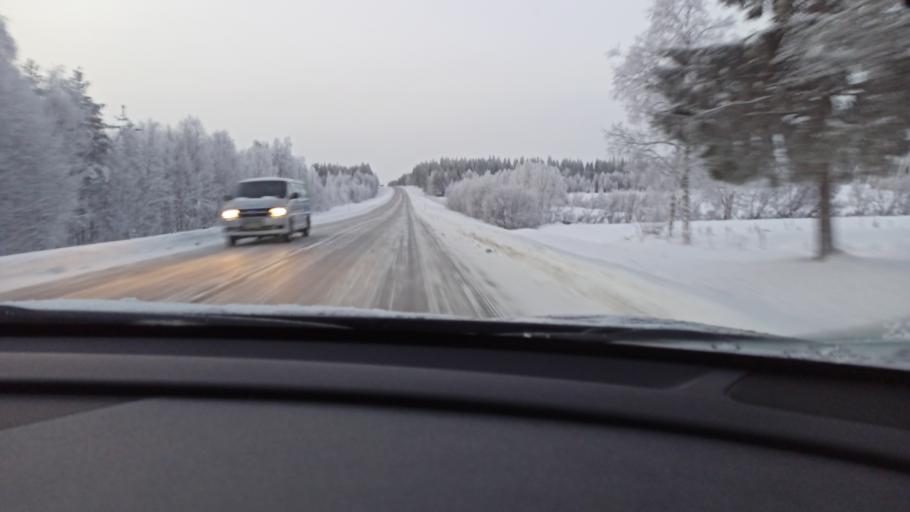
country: FI
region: Lapland
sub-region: Pohjois-Lappi
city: Sodankylae
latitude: 66.9838
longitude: 26.3338
